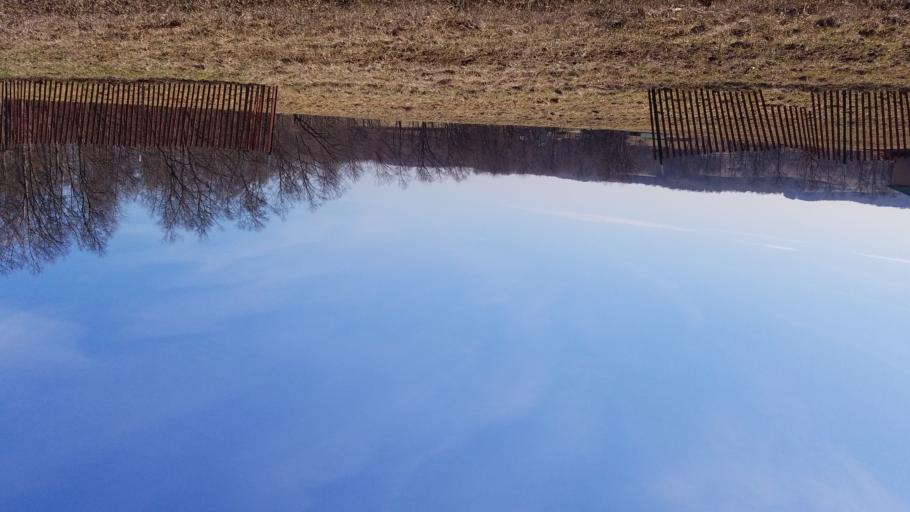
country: US
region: Ohio
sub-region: Knox County
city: Fredericktown
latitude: 40.5039
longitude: -82.4465
